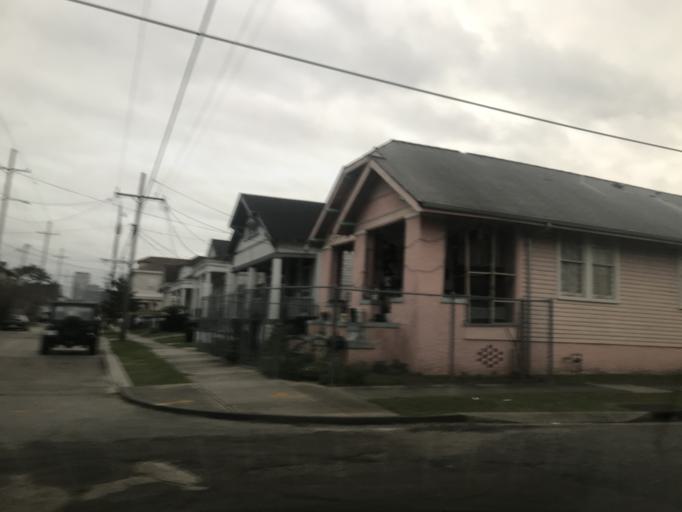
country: US
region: Louisiana
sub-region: Orleans Parish
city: New Orleans
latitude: 29.9665
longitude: -90.0929
